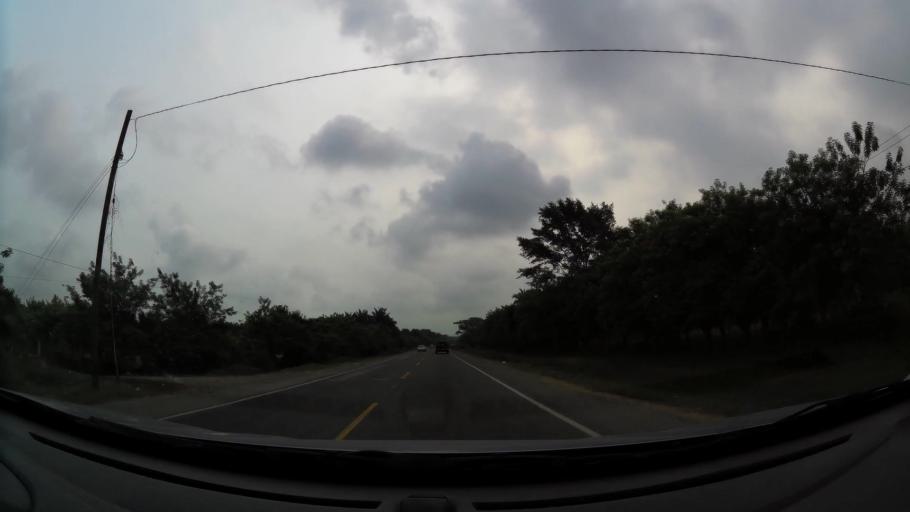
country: HN
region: Yoro
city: Guaimitas
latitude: 15.4898
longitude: -87.7553
